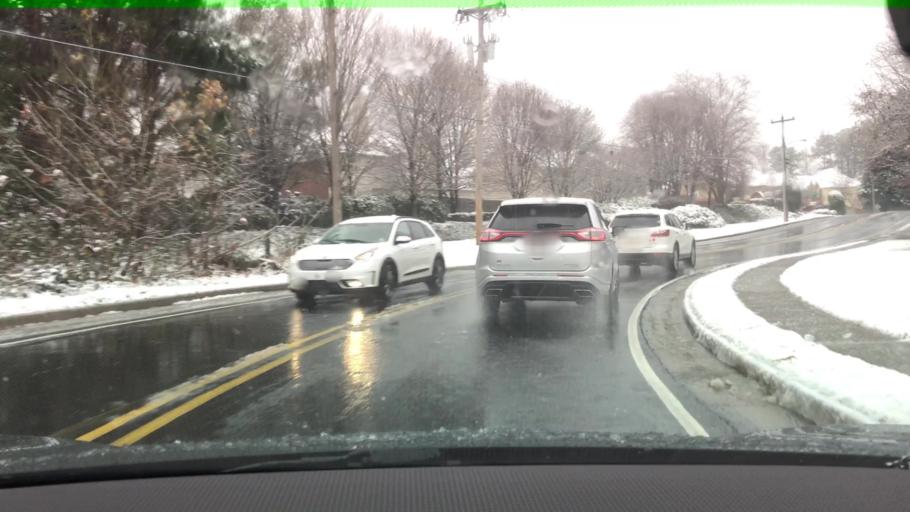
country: US
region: Georgia
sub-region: Gwinnett County
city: Suwanee
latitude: 34.0109
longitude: -84.0733
